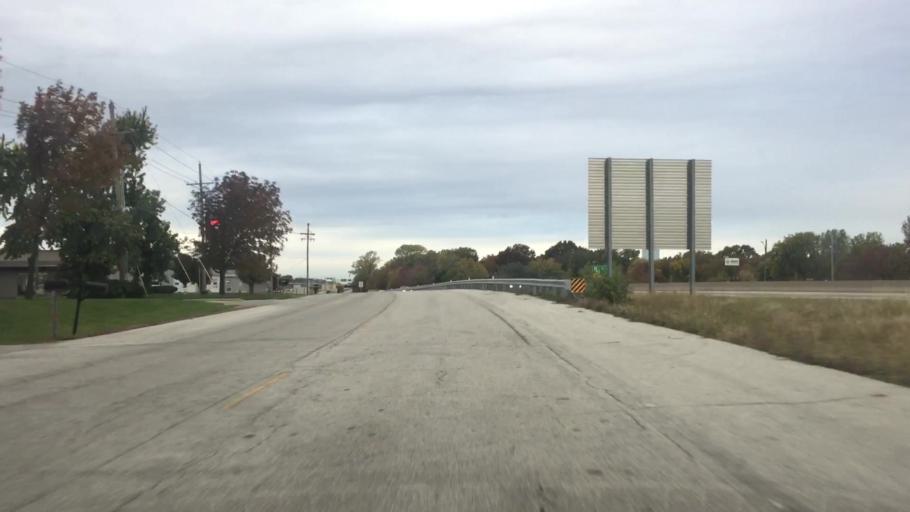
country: US
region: Missouri
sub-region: Jackson County
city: Lees Summit
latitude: 38.9025
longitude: -94.3661
